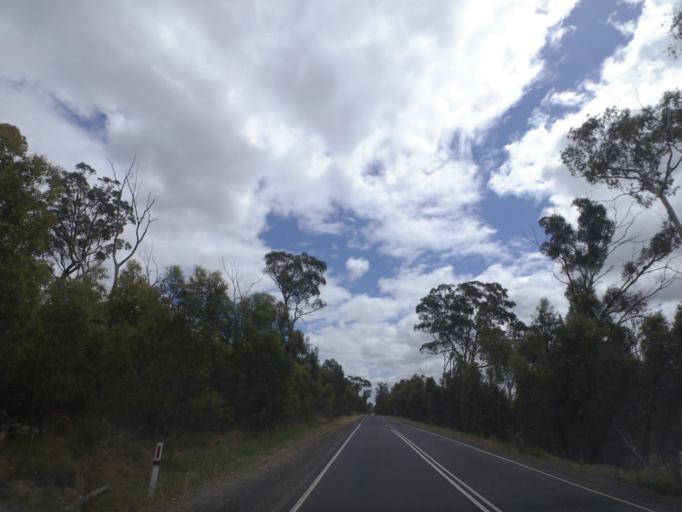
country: AU
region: Victoria
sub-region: Whittlesea
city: Whittlesea
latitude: -37.2732
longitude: 145.0511
